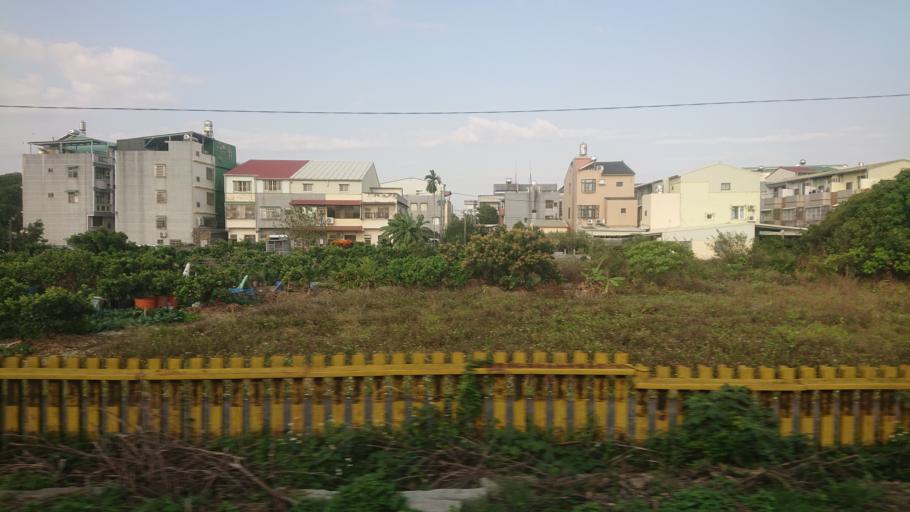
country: TW
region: Taiwan
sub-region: Chiayi
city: Jiayi Shi
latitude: 23.5506
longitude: 120.4304
